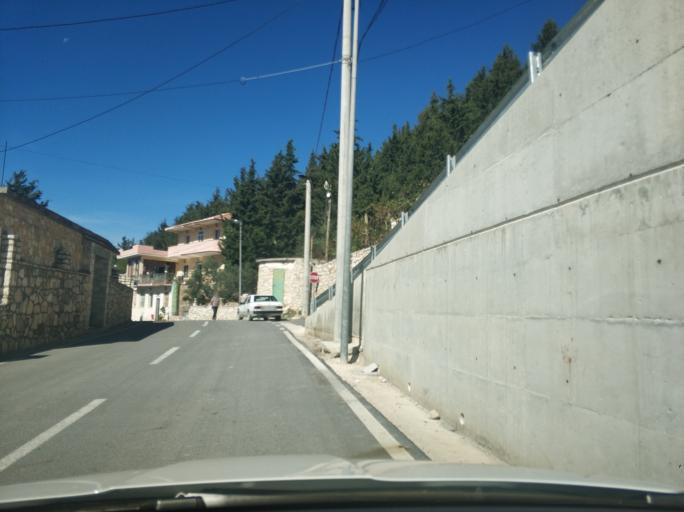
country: AL
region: Vlore
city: Vlore
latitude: 40.4430
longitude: 19.5206
